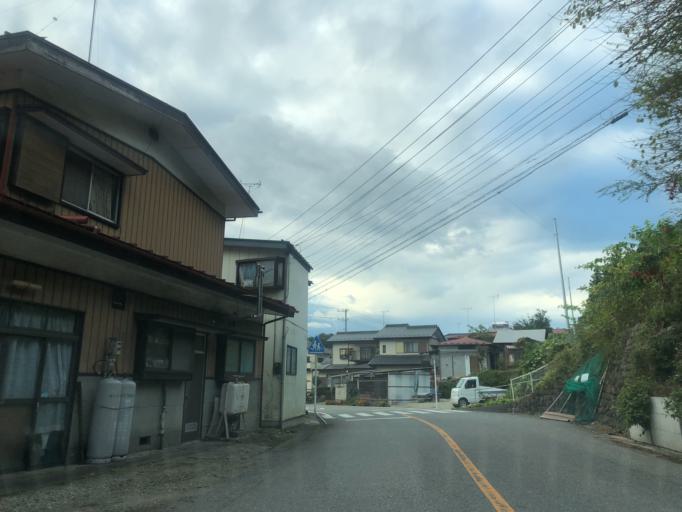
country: JP
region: Tochigi
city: Kuroiso
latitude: 36.9441
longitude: 140.1068
